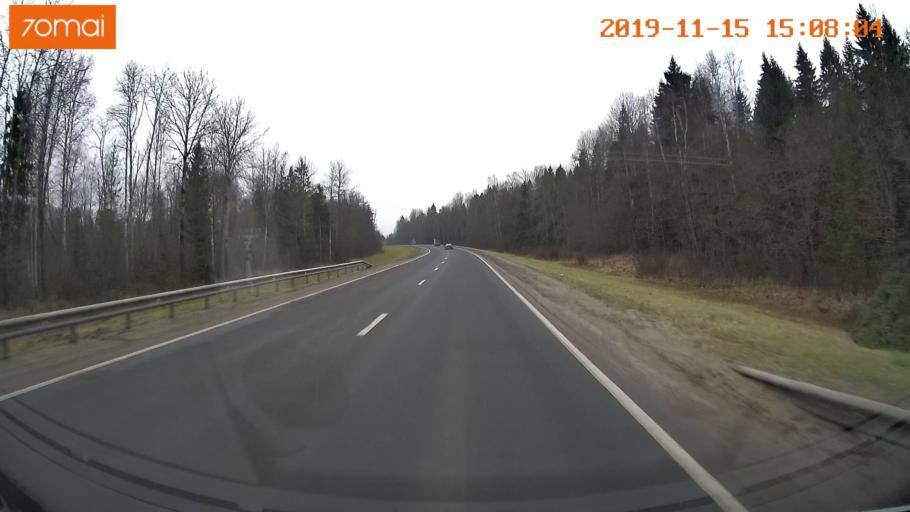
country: RU
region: Jaroslavl
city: Prechistoye
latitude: 58.3760
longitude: 40.2825
